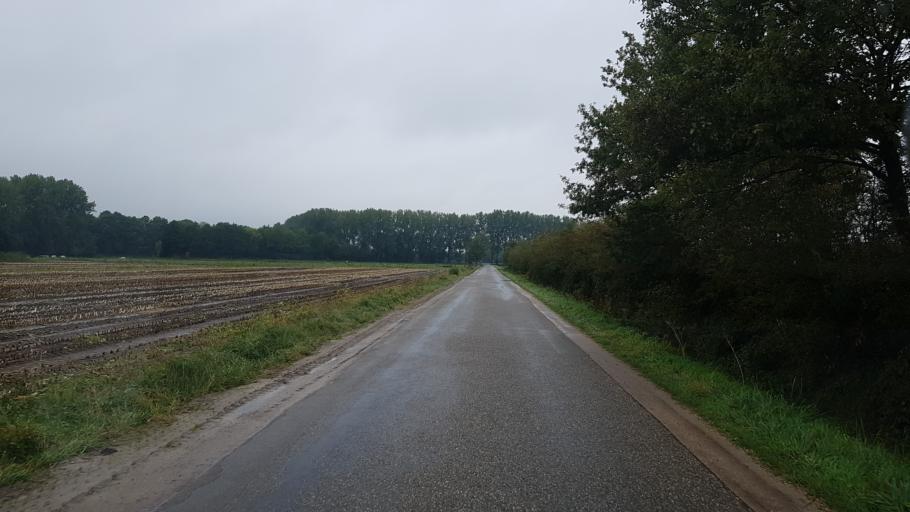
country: NL
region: Gelderland
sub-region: Gemeente Apeldoorn
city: Loenen
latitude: 52.1702
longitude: 6.0316
